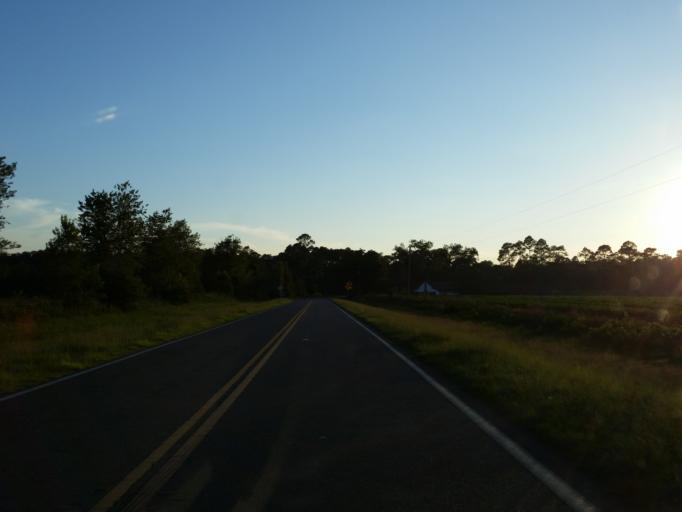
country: US
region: Georgia
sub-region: Berrien County
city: Nashville
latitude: 31.1861
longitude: -83.1850
